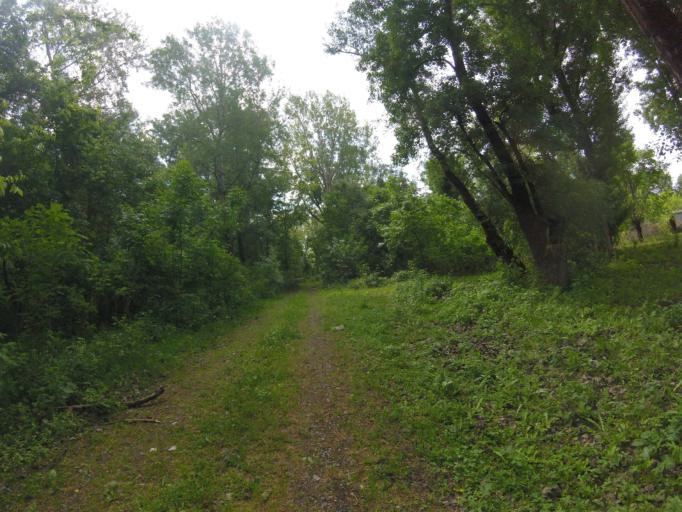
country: HU
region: Borsod-Abauj-Zemplen
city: Tokaj
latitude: 48.1300
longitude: 21.4150
